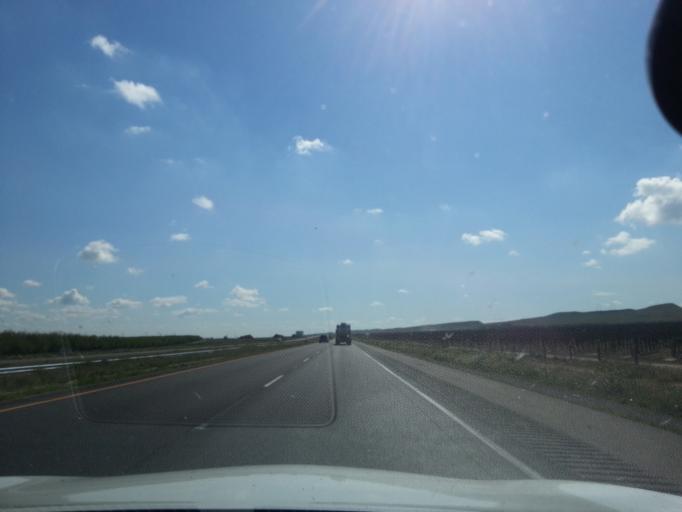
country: US
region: California
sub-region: Fresno County
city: Coalinga
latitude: 36.3609
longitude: -120.3274
